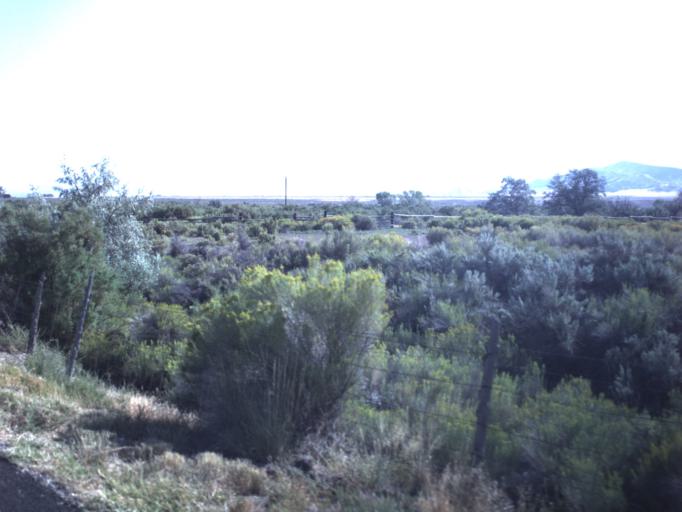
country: US
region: Utah
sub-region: Sevier County
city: Salina
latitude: 39.0159
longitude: -111.8526
